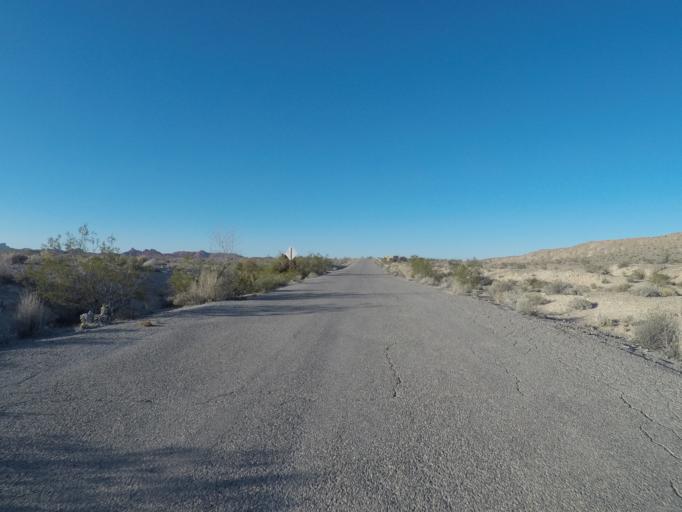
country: US
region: Nevada
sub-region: Clark County
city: Moapa Valley
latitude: 36.3915
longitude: -114.4227
